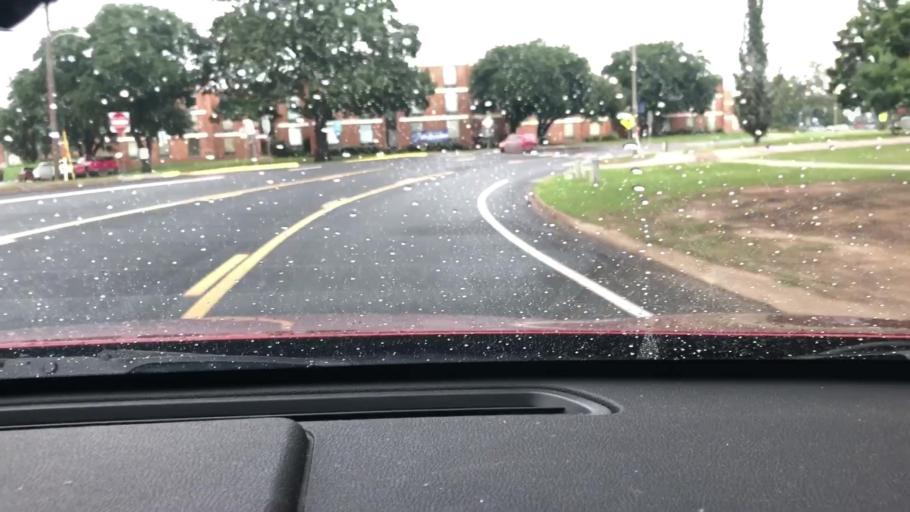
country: US
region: Arkansas
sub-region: Columbia County
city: Magnolia
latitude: 33.2927
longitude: -93.2374
